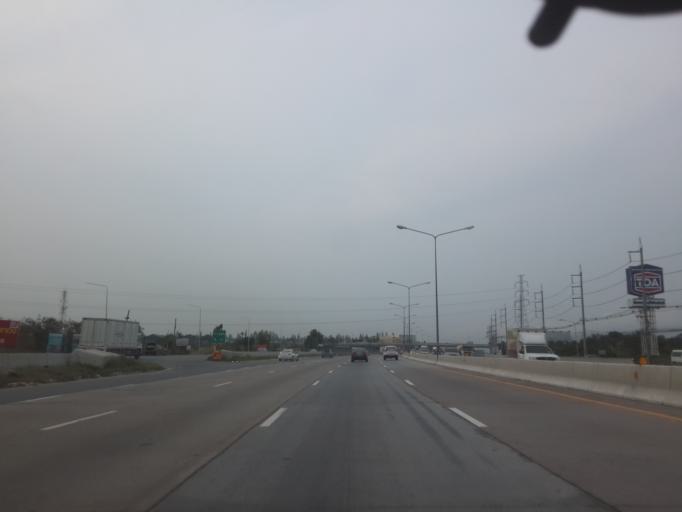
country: TH
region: Chon Buri
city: Si Racha
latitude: 13.1499
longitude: 100.9859
